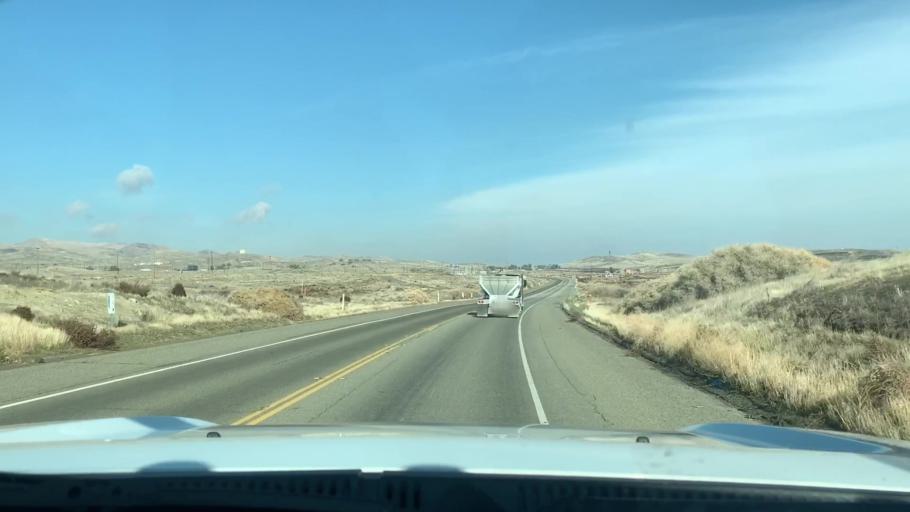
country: US
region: California
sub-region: Fresno County
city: Coalinga
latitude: 36.2280
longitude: -120.3136
